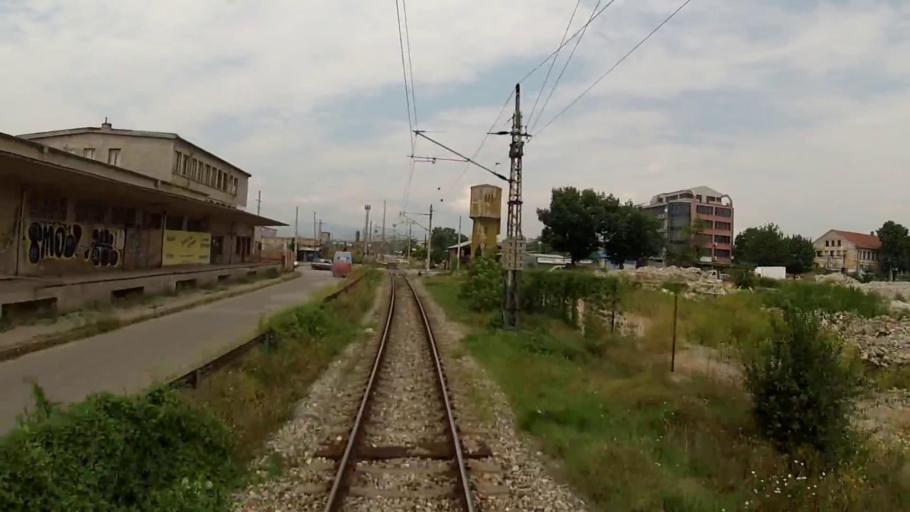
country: BG
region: Blagoevgrad
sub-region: Obshtina Blagoevgrad
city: Blagoevgrad
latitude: 42.0009
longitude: 23.0895
